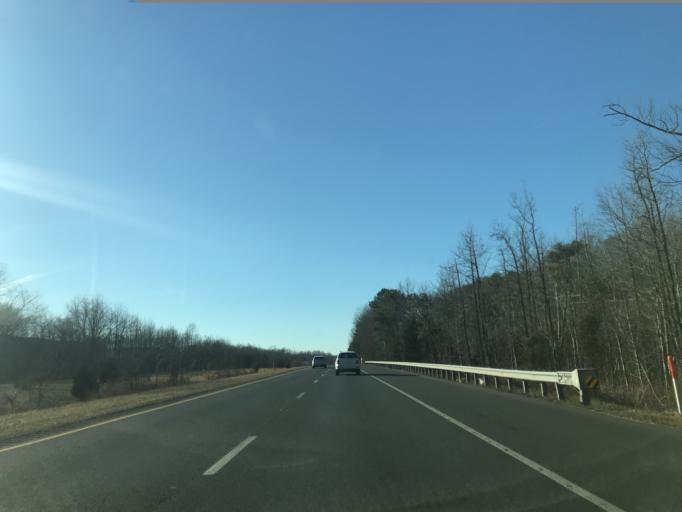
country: US
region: Maryland
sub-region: Prince George's County
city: Mellwood
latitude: 38.8178
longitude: -76.8384
